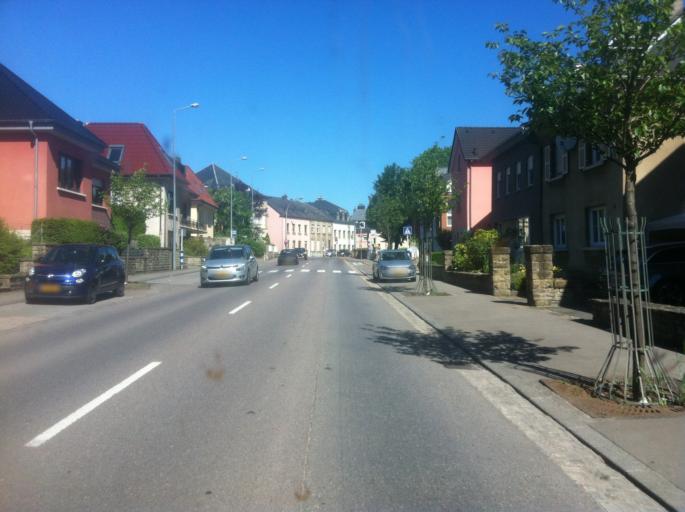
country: LU
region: Grevenmacher
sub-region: Canton d'Echternach
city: Echternach
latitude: 49.8097
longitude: 6.4255
